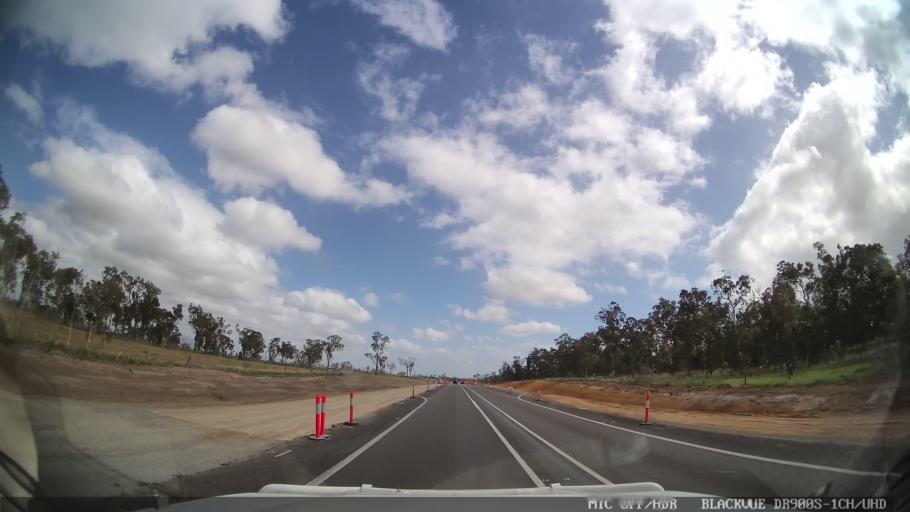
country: AU
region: Queensland
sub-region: Whitsunday
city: Red Hill
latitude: -20.2950
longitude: 148.5029
